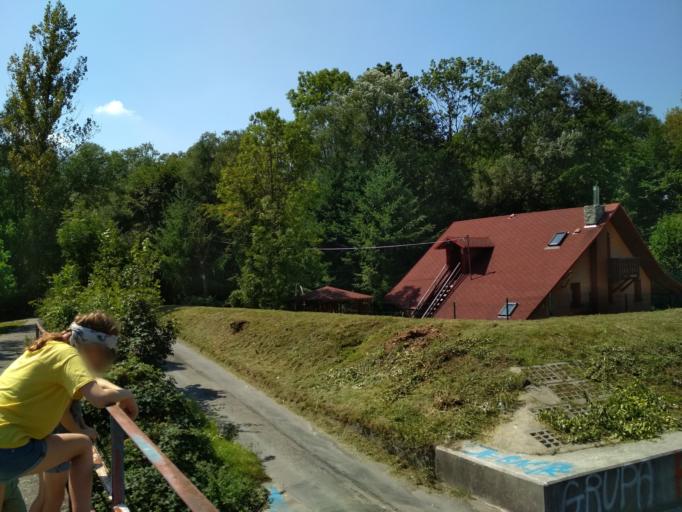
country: PL
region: Silesian Voivodeship
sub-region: Powiat cieszynski
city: Brenna
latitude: 49.7326
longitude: 18.8953
